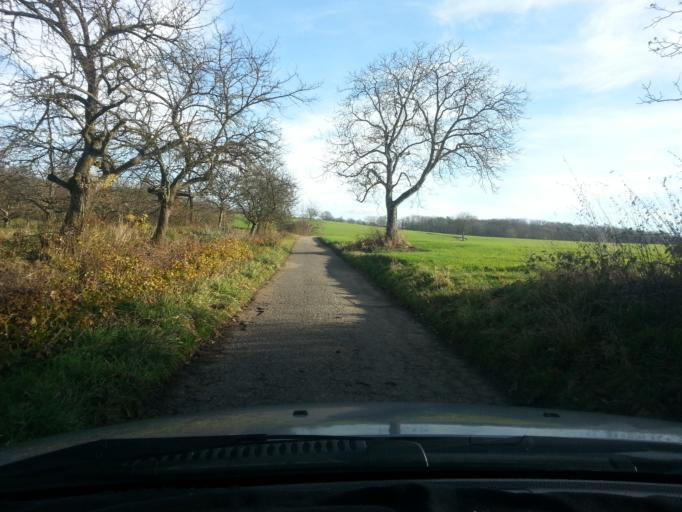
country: DE
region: Baden-Wuerttemberg
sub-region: Karlsruhe Region
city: Ostringen
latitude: 49.1997
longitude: 8.7034
